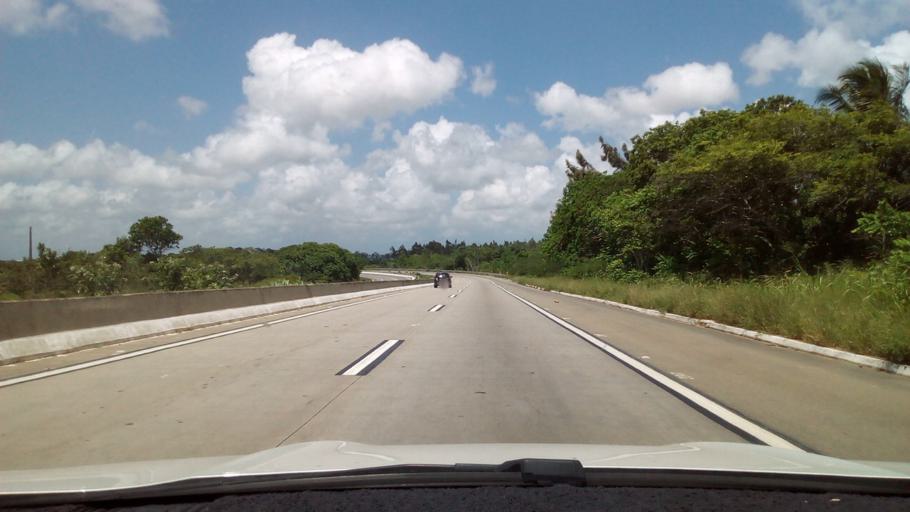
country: BR
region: Paraiba
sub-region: Conde
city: Conde
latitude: -7.2997
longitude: -34.9383
